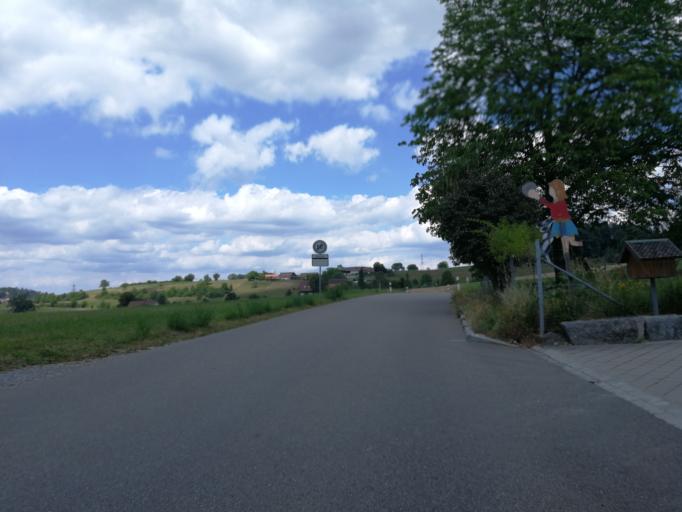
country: CH
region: Zurich
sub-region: Bezirk Hinwil
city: Gruet
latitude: 47.2970
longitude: 8.7876
